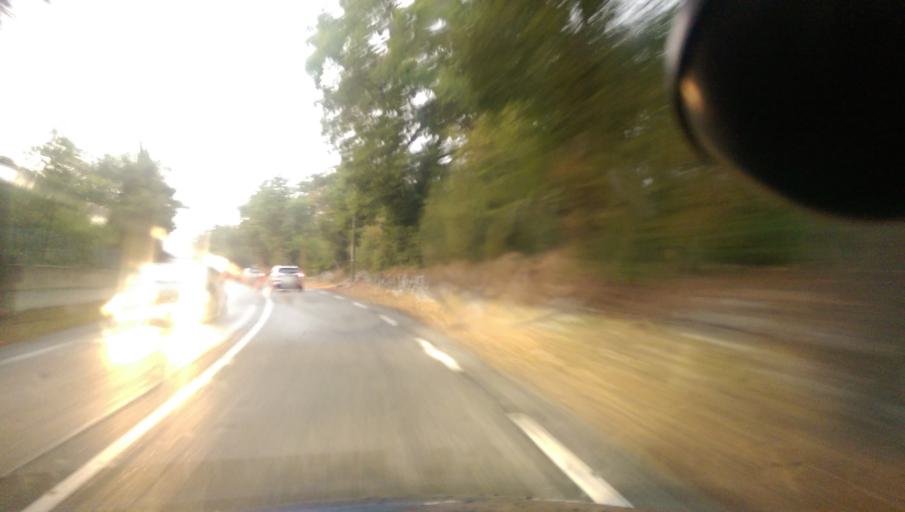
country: FR
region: Provence-Alpes-Cote d'Azur
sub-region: Departement des Alpes-Maritimes
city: Saint-Vallier-de-Thiey
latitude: 43.6881
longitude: 6.8737
